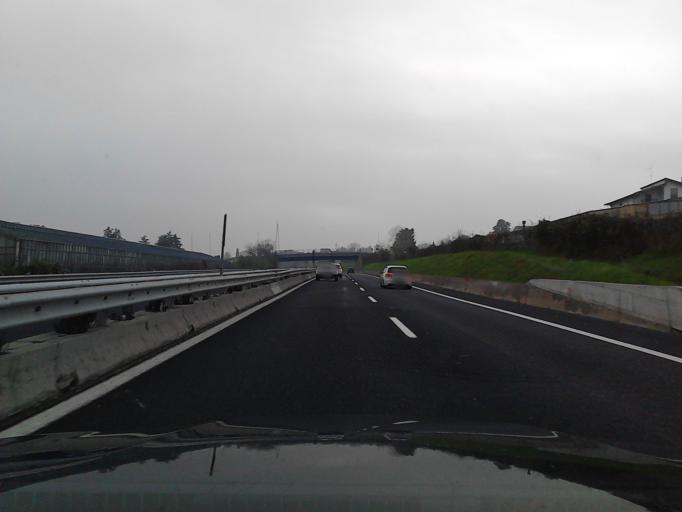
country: IT
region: Abruzzo
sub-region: Provincia di Pescara
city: San Martino Bassa
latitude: 42.5149
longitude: 14.1283
